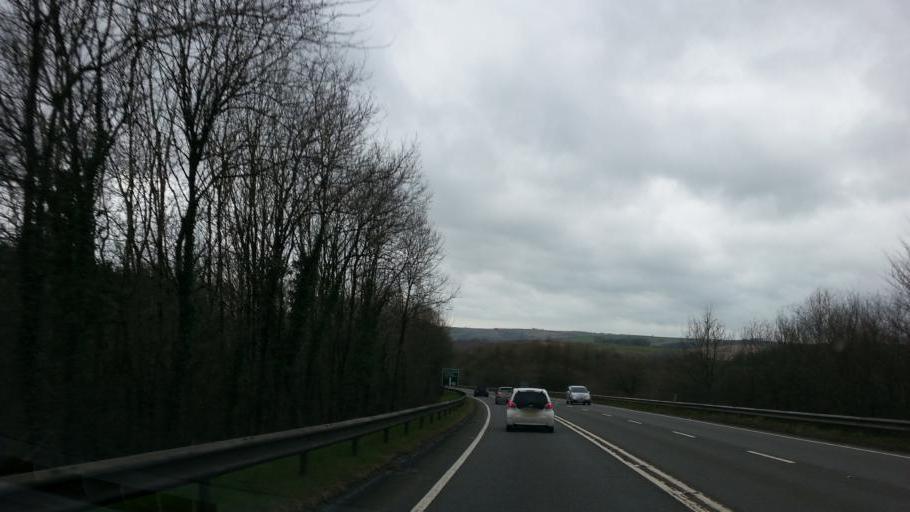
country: GB
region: England
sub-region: Devon
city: South Molton
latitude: 51.0102
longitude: -3.7539
